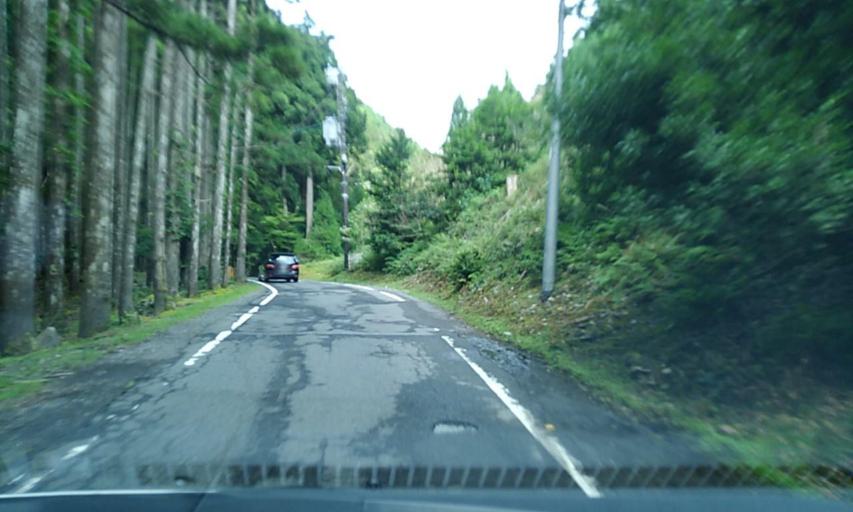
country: JP
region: Shiga Prefecture
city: Kitahama
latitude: 35.2700
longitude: 135.8605
